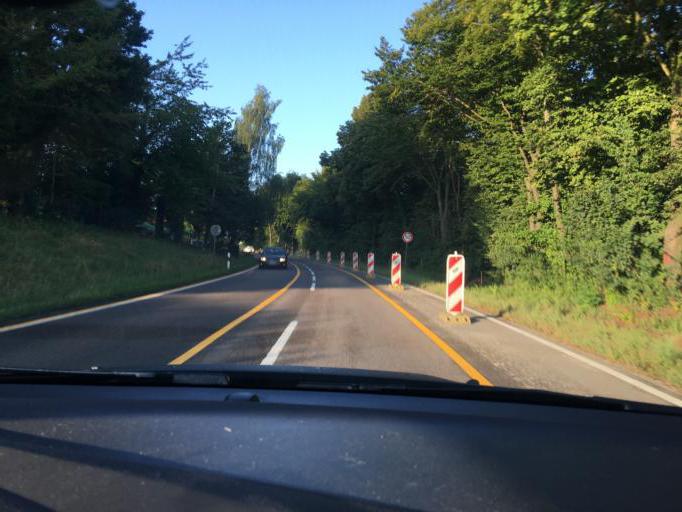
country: DE
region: Bavaria
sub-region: Upper Bavaria
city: Erding
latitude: 48.3012
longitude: 11.9161
